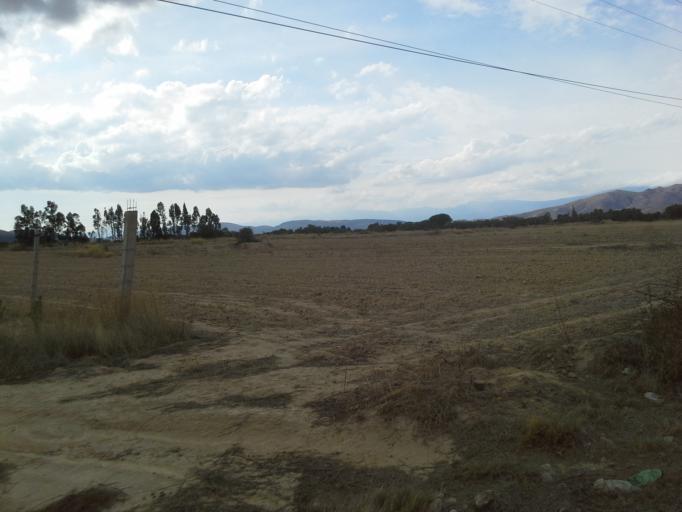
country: BO
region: Cochabamba
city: Tarata
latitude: -17.5922
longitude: -66.0187
